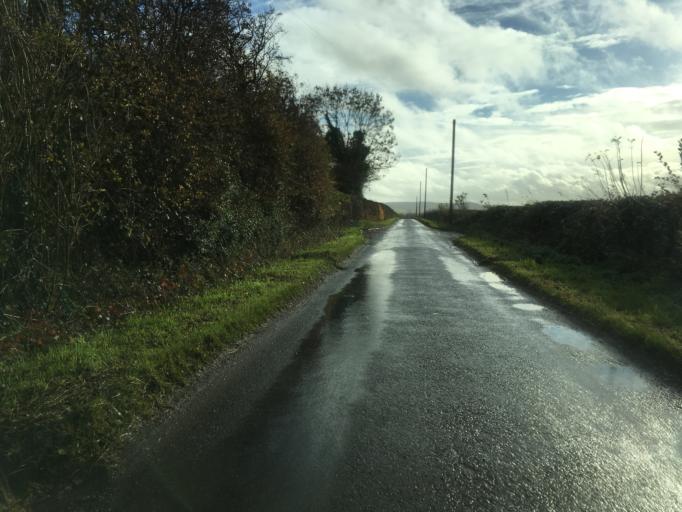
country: GB
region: England
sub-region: South Gloucestershire
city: Pucklechurch
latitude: 51.4864
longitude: -2.4104
